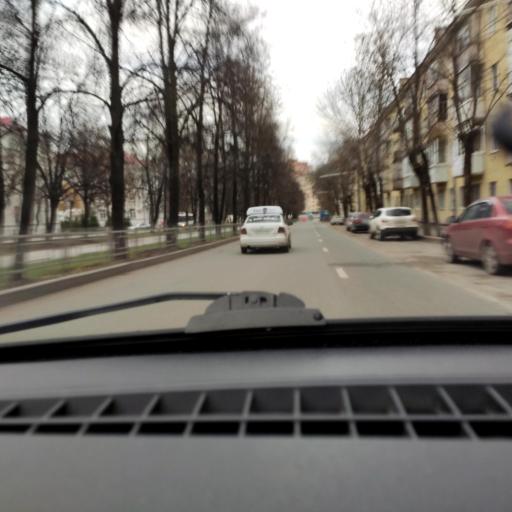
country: RU
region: Bashkortostan
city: Ufa
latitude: 54.8173
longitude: 56.1021
